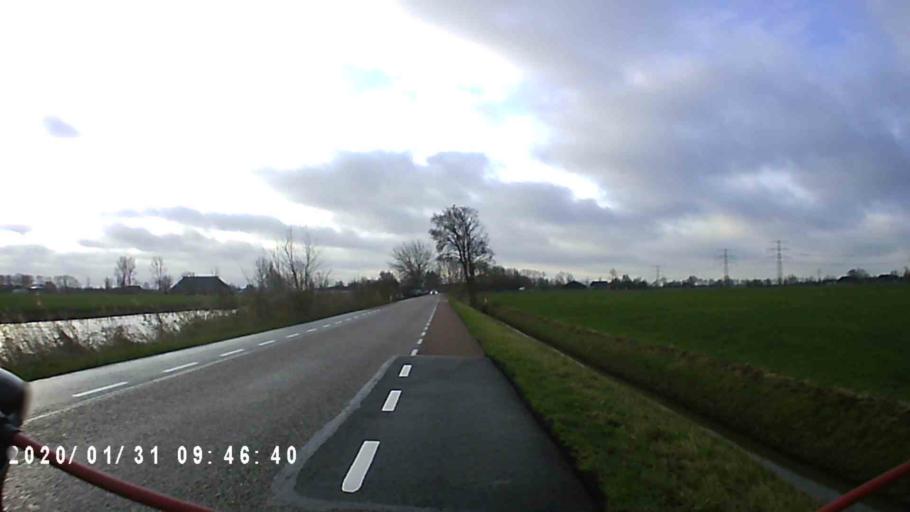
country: NL
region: Groningen
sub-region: Gemeente Zuidhorn
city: Aduard
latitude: 53.2654
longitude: 6.4830
